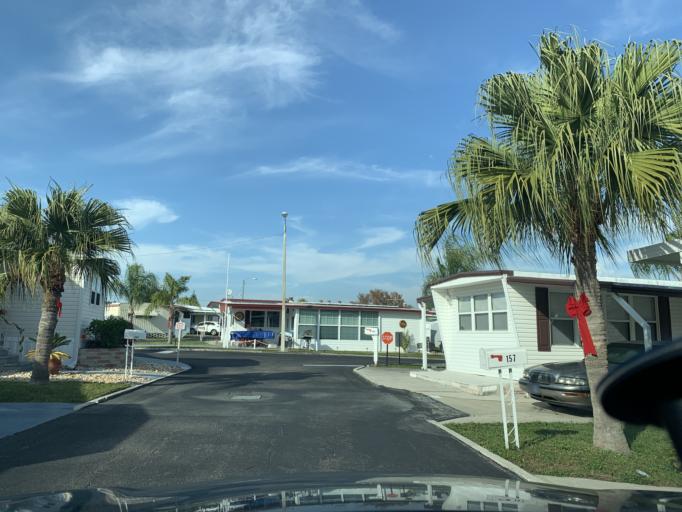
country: US
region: Florida
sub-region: Pinellas County
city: Largo
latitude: 27.8982
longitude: -82.7852
